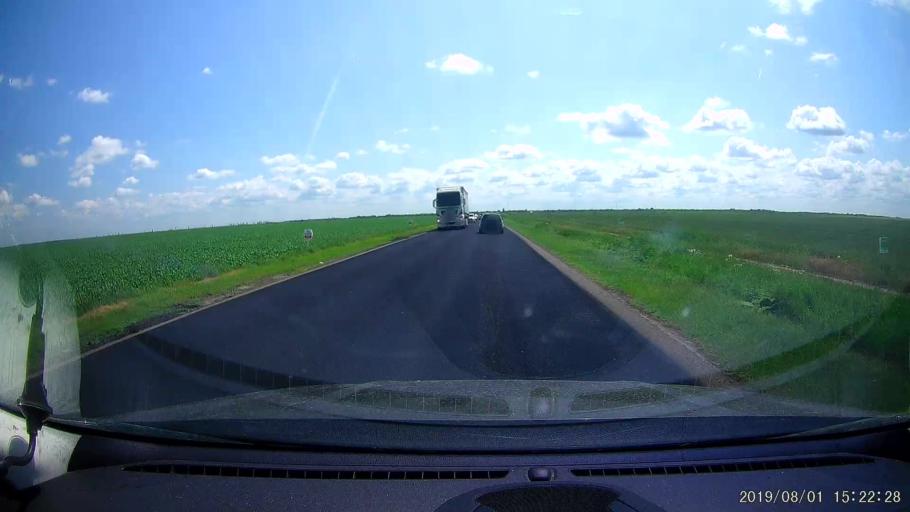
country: RO
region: Braila
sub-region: Comuna Viziru
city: Lanurile
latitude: 45.0531
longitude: 27.7755
